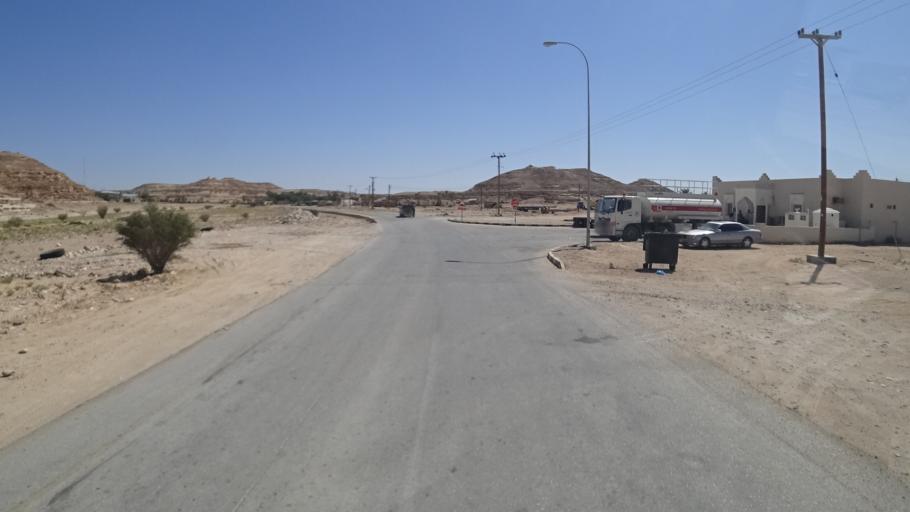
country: OM
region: Zufar
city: Salalah
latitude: 17.4833
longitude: 53.3491
